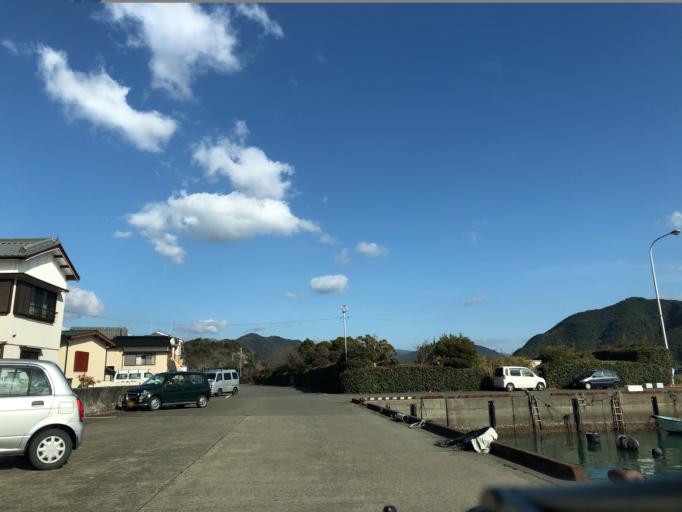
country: JP
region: Kochi
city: Sukumo
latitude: 32.9150
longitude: 132.7043
